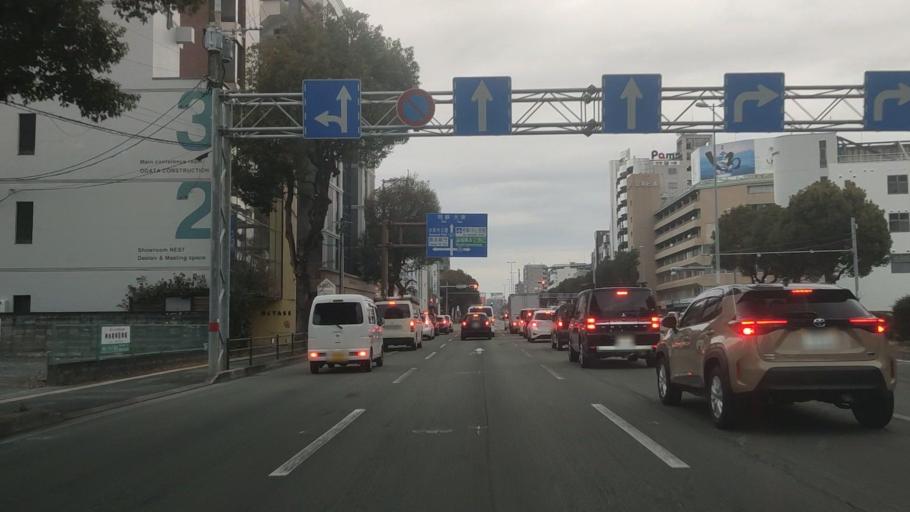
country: JP
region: Kumamoto
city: Kumamoto
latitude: 32.7869
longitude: 130.7465
